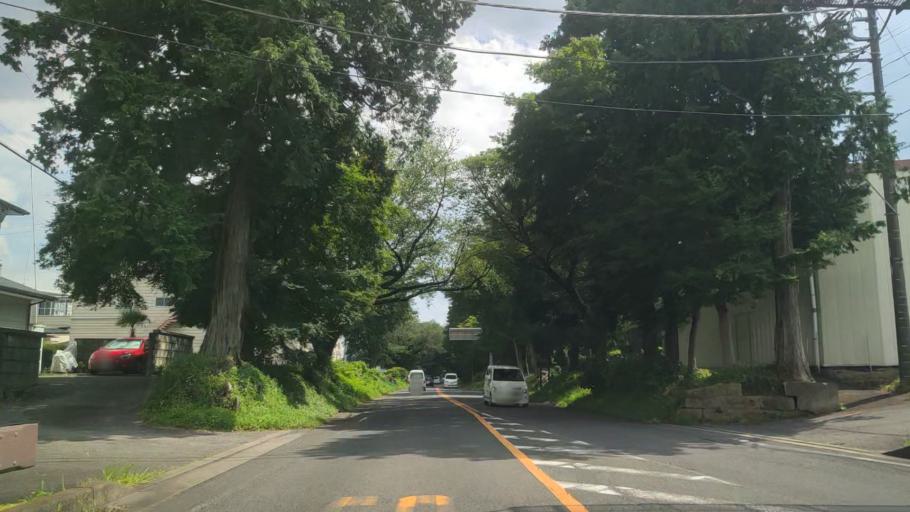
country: JP
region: Tochigi
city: Utsunomiya-shi
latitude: 36.6244
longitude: 139.8527
